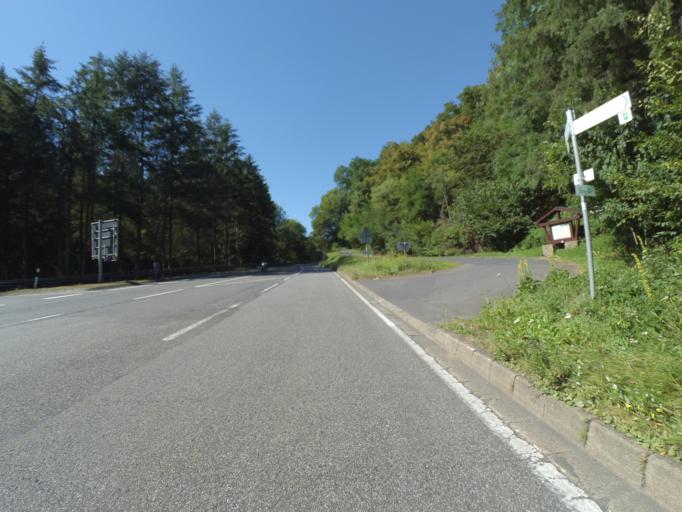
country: DE
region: Rheinland-Pfalz
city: Bad Bertrich
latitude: 50.0746
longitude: 7.0201
